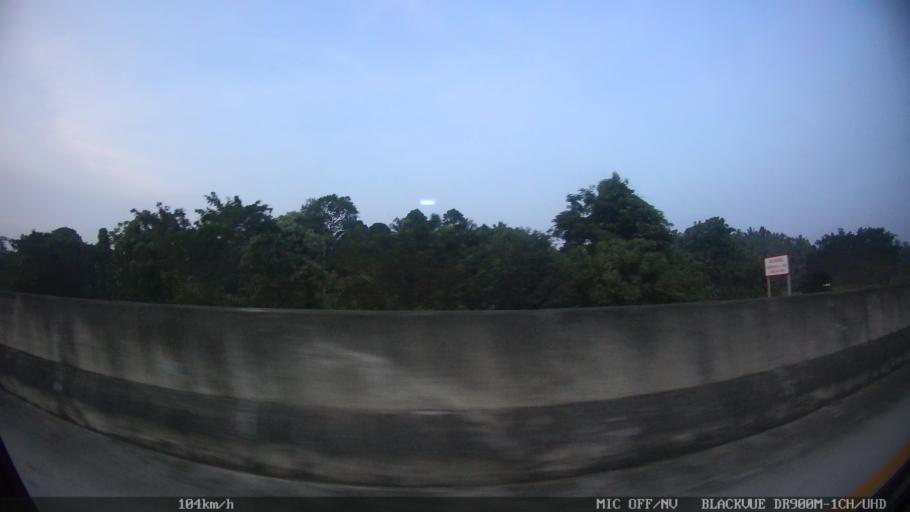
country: ID
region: Lampung
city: Kalianda
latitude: -5.7016
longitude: 105.6338
